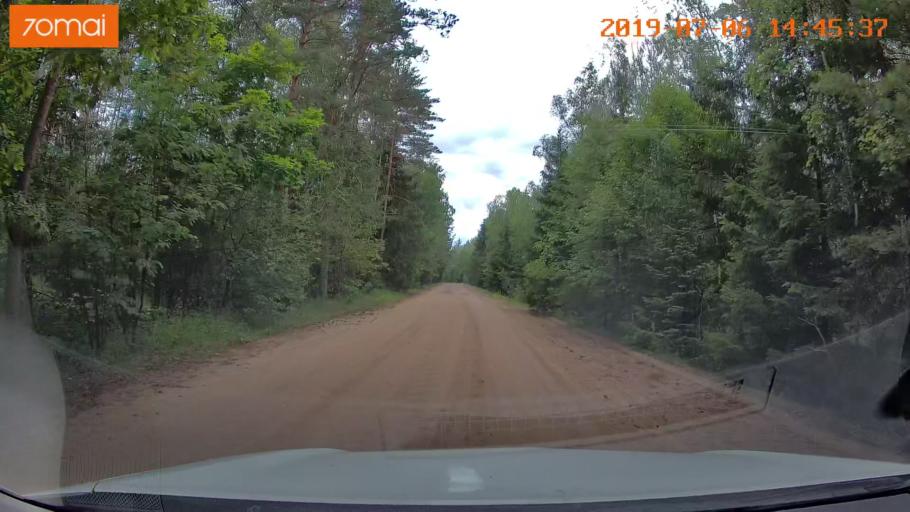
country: BY
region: Minsk
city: Ivyanyets
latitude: 53.9737
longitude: 26.6856
